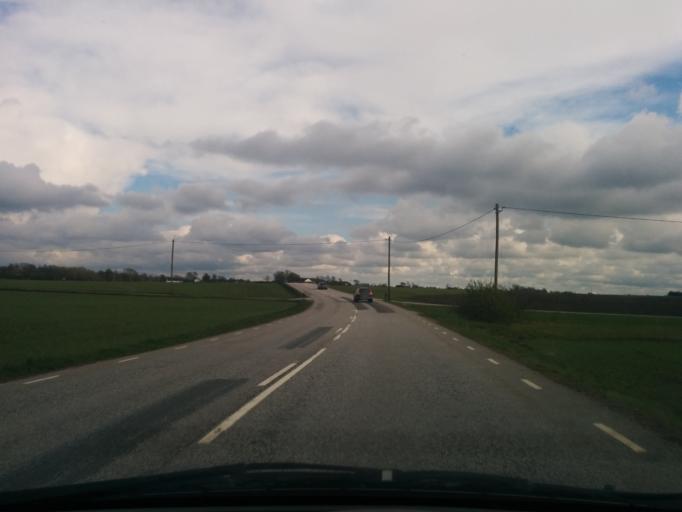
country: SE
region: Skane
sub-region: Svedala Kommun
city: Klagerup
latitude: 55.6380
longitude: 13.2779
